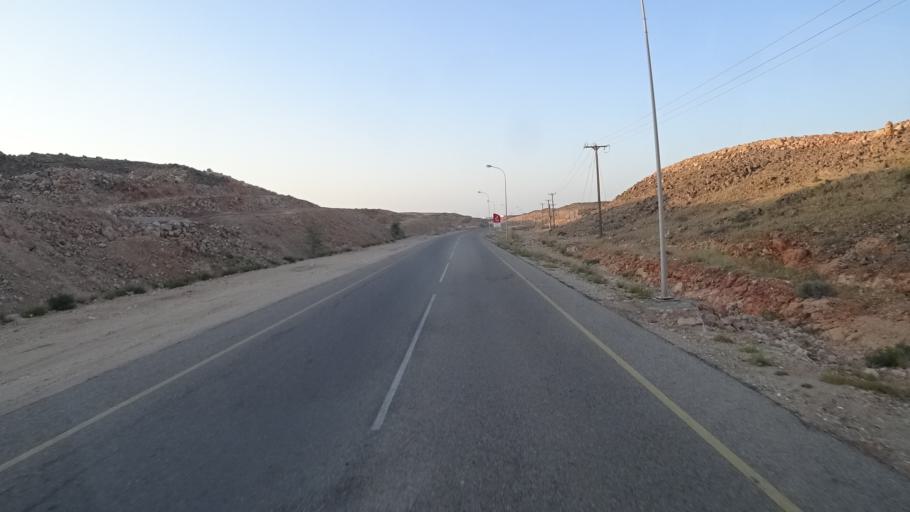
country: OM
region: Ash Sharqiyah
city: Sur
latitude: 22.5006
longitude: 59.7916
